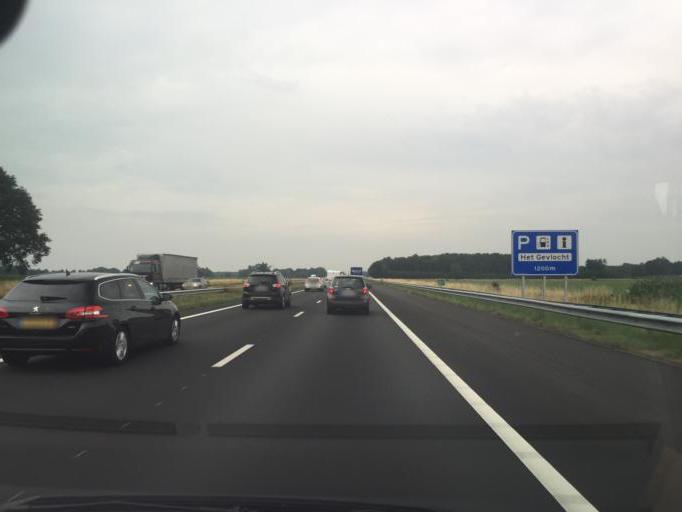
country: NL
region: North Brabant
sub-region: Gemeente Asten
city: Asten
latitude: 51.4113
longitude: 5.7912
